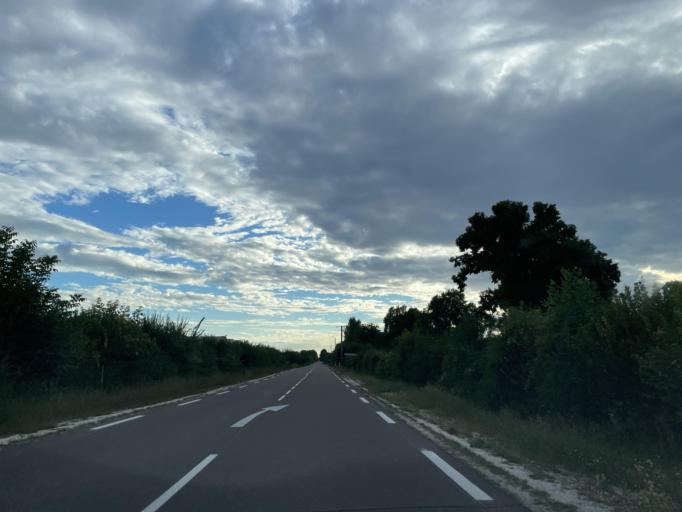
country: FR
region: Ile-de-France
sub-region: Departement de Seine-et-Marne
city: Gouaix
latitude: 48.4311
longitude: 3.3182
